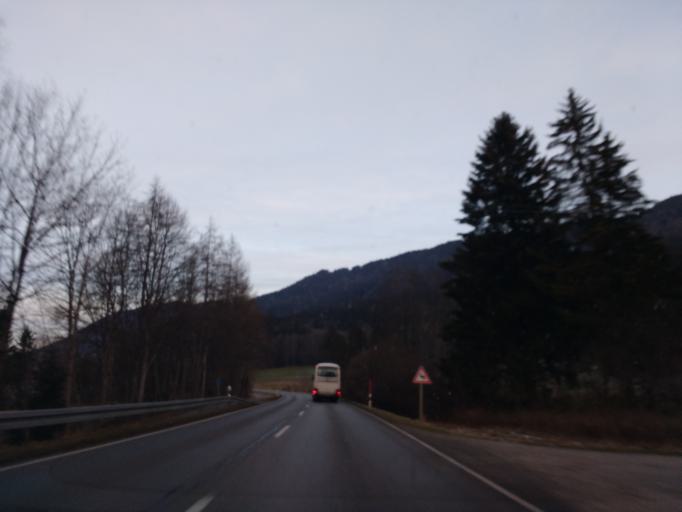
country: DE
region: Bavaria
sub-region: Swabia
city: Schwangau
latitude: 47.5927
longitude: 10.7784
